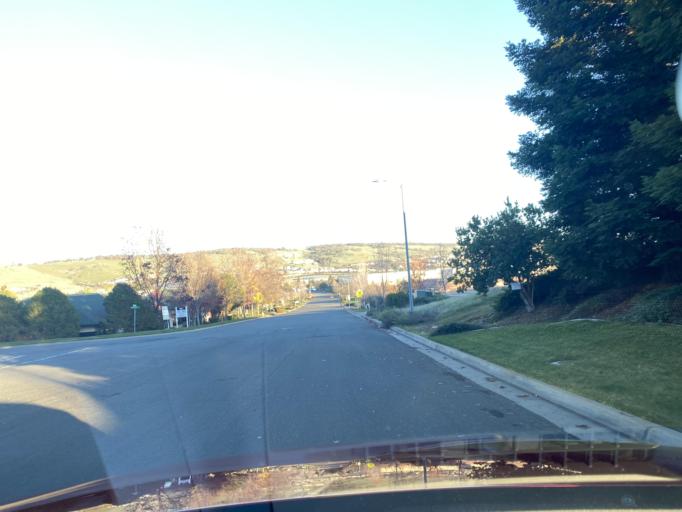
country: US
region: California
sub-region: El Dorado County
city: El Dorado Hills
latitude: 38.6352
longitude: -121.0715
